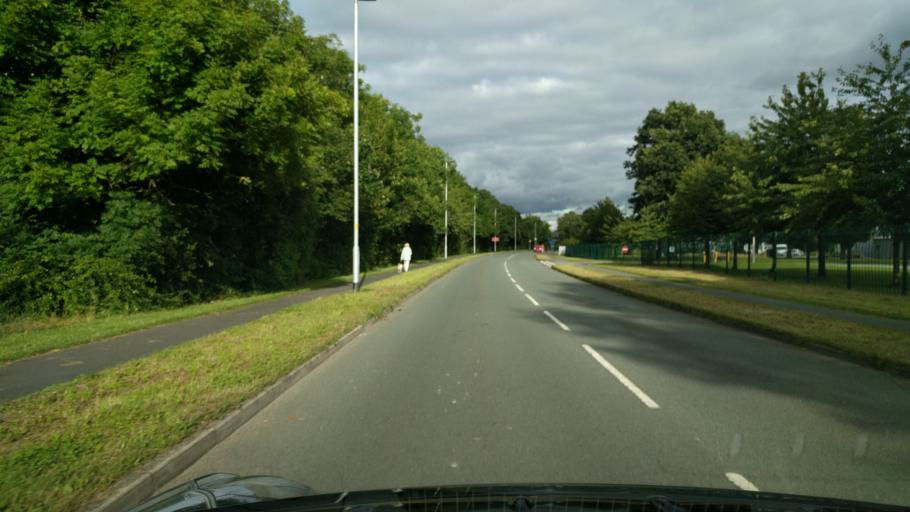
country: GB
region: England
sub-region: Warrington
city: Croft
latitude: 53.4174
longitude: -2.5496
